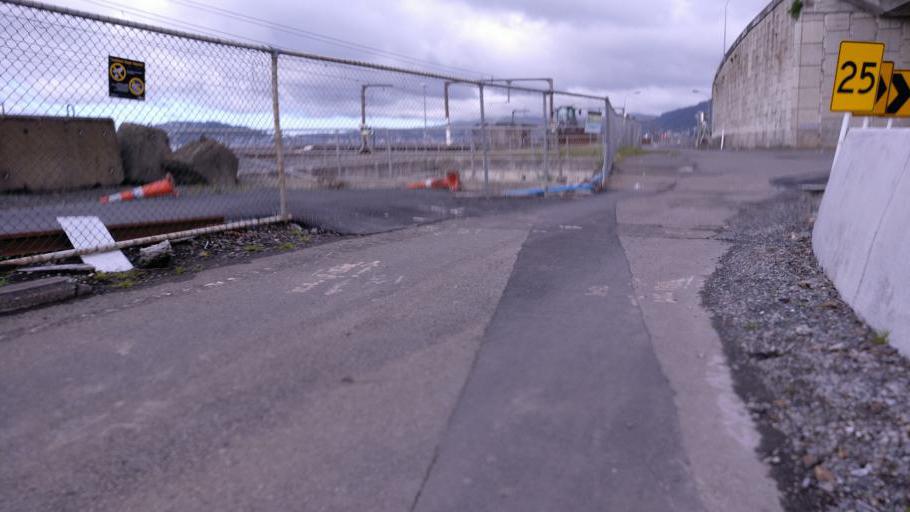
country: NZ
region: Wellington
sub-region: Wellington City
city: Wellington
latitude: -41.2480
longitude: 174.8144
